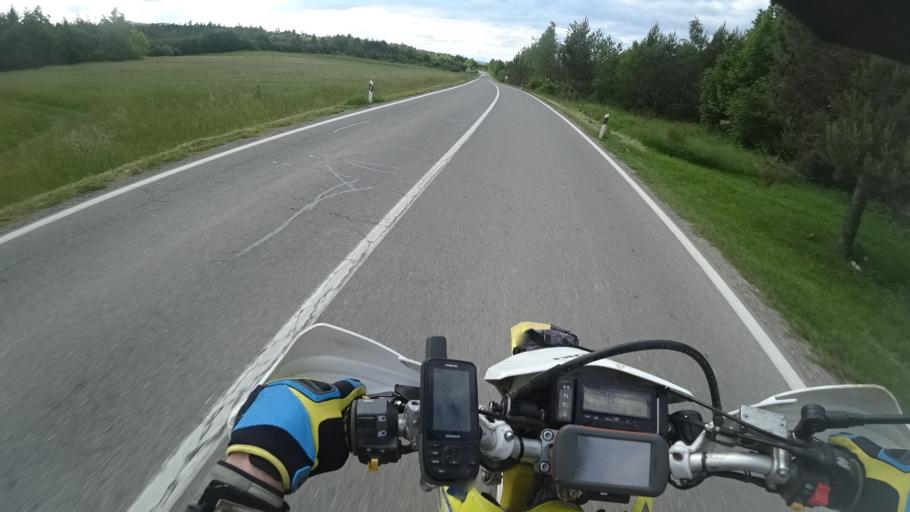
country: HR
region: Licko-Senjska
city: Gospic
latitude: 44.5226
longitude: 15.4142
